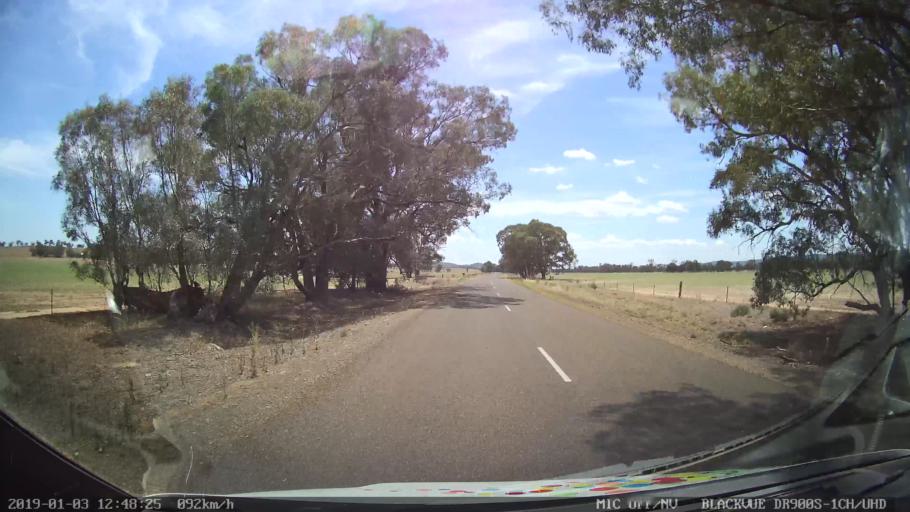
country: AU
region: New South Wales
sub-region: Weddin
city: Grenfell
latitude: -33.7149
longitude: 148.2502
